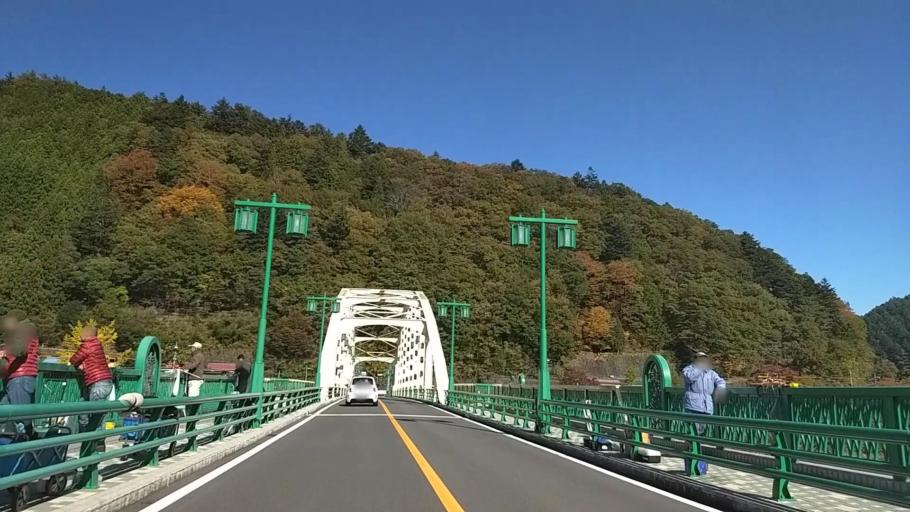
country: JP
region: Yamanashi
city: Otsuki
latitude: 35.7744
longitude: 138.9990
